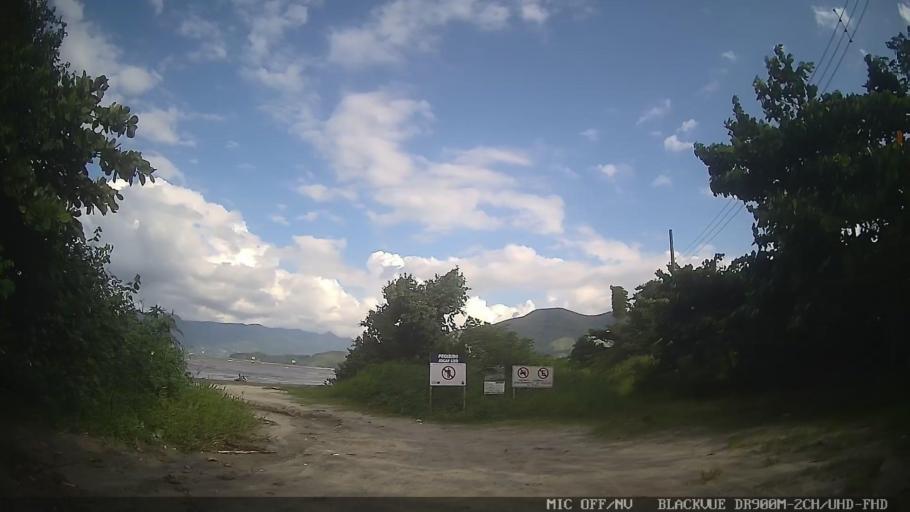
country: BR
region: Sao Paulo
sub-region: Sao Sebastiao
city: Sao Sebastiao
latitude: -23.7053
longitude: -45.4274
